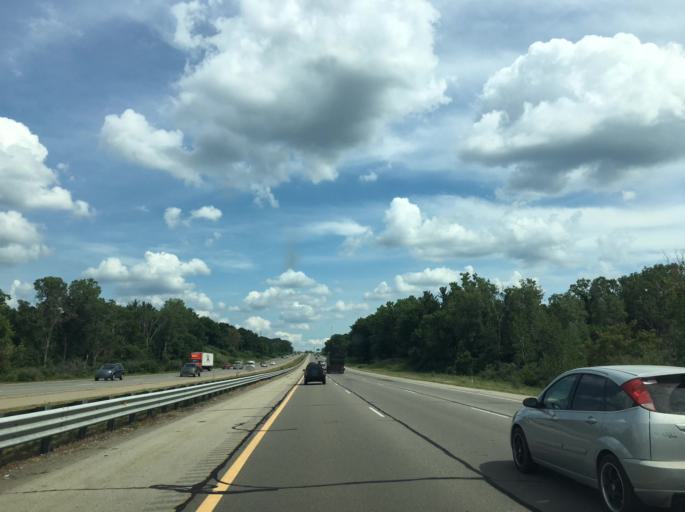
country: US
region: Michigan
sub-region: Oakland County
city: Holly
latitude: 42.7995
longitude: -83.5544
